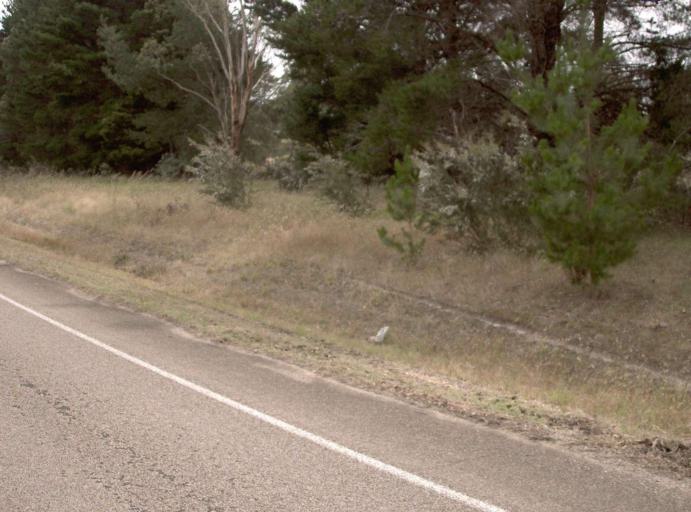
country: AU
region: Victoria
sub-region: Wellington
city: Sale
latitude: -37.9271
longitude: 147.0895
